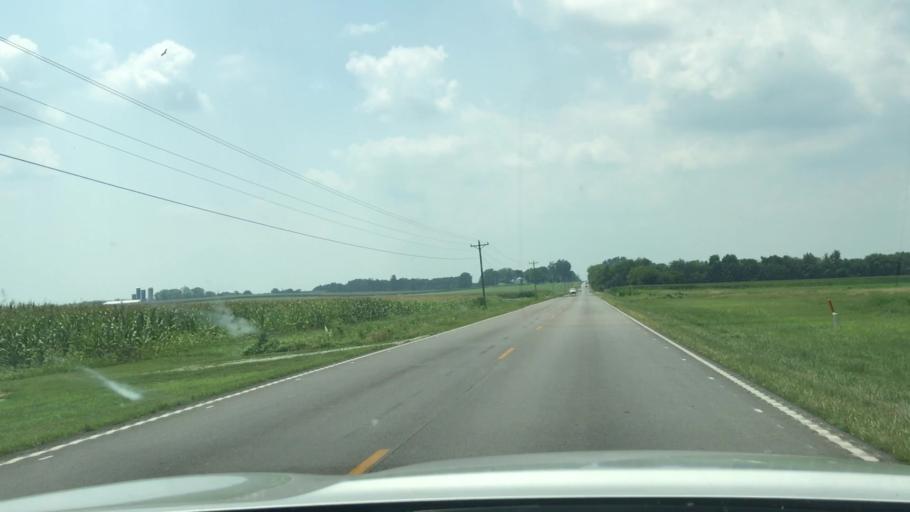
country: US
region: Kentucky
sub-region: Todd County
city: Guthrie
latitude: 36.6842
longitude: -87.1407
